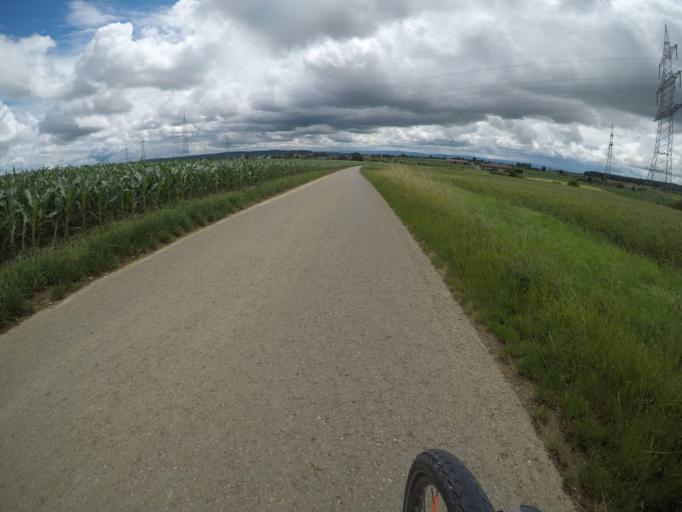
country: DE
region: Baden-Wuerttemberg
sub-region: Regierungsbezirk Stuttgart
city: Deckenpfronn
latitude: 48.6169
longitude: 8.8246
